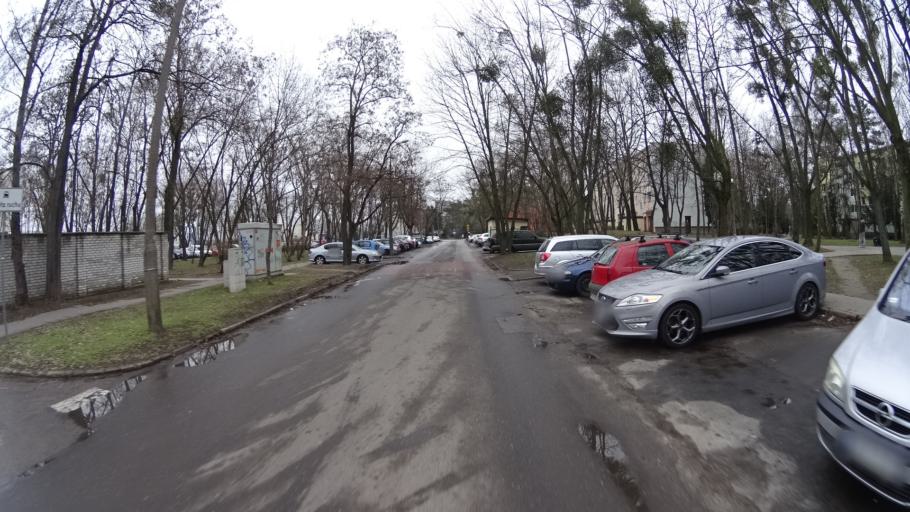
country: PL
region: Masovian Voivodeship
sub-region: Warszawa
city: Bemowo
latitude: 52.2380
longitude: 20.9019
